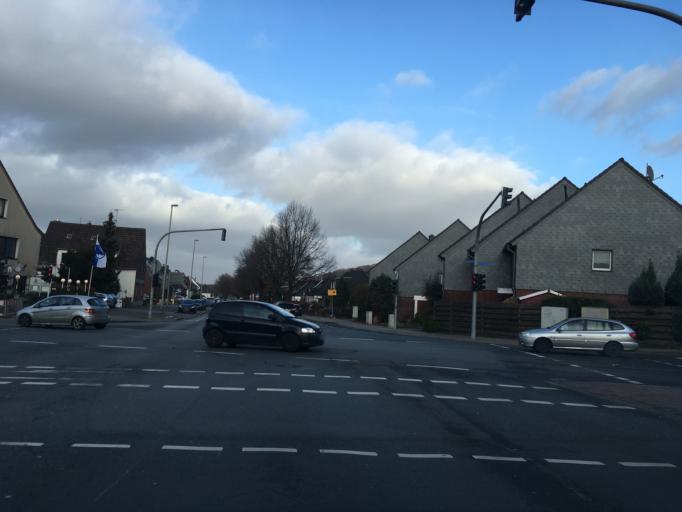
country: DE
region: North Rhine-Westphalia
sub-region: Regierungsbezirk Munster
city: Bottrop
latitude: 51.5409
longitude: 6.8656
